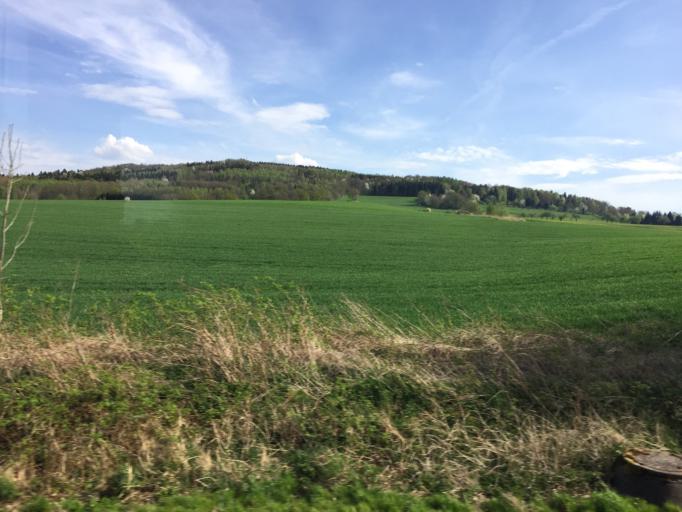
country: DE
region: Saxony
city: Sohland am Rotstein
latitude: 51.1214
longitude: 14.7448
